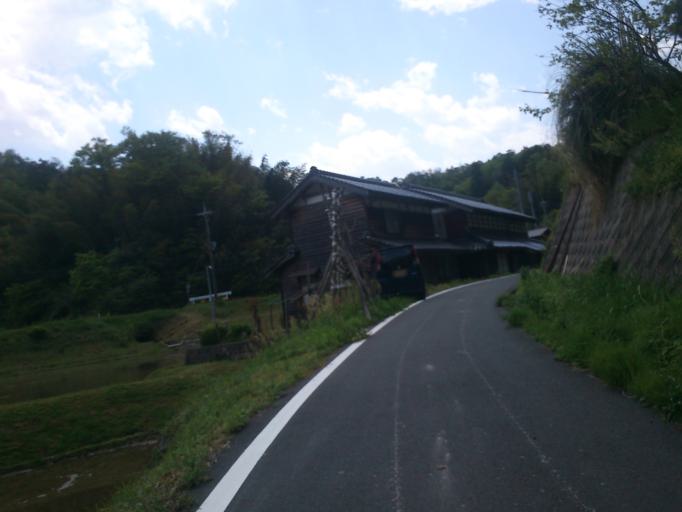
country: JP
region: Kyoto
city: Miyazu
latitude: 35.6931
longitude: 135.1351
